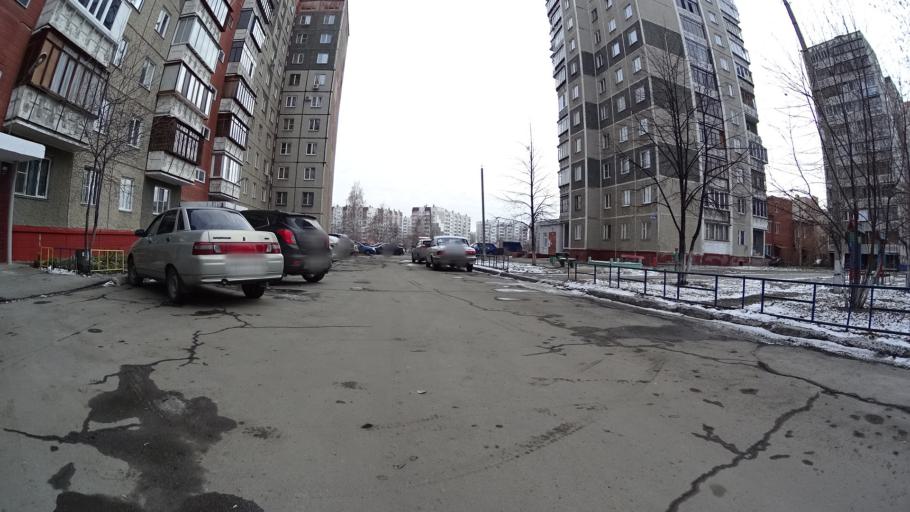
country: RU
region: Chelyabinsk
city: Roshchino
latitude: 55.1876
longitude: 61.3007
